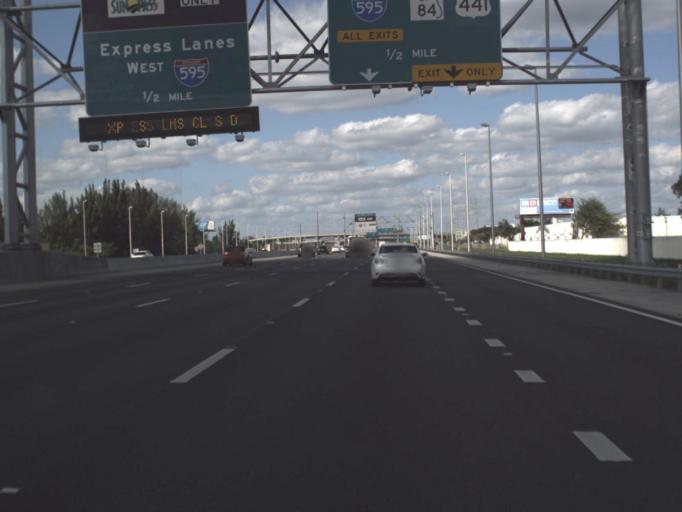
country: US
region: Florida
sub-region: Broward County
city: Davie
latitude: 26.0728
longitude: -80.2155
